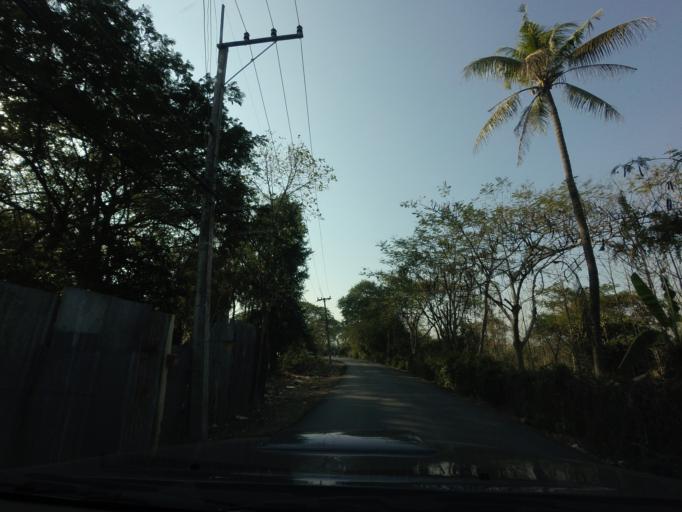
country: TH
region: Chiang Mai
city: San Sai
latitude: 18.9208
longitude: 98.9643
